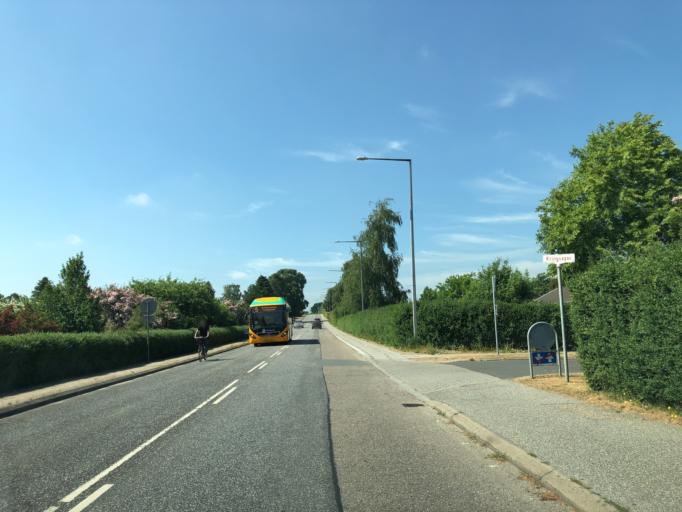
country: DK
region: South Denmark
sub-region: Kolding Kommune
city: Kolding
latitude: 55.5174
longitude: 9.4842
